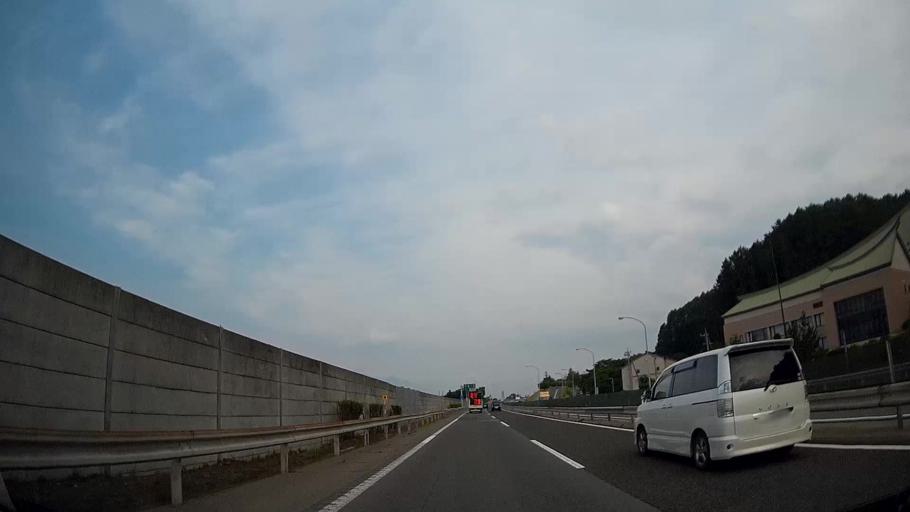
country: JP
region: Nagano
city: Okaya
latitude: 36.0297
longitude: 138.0720
